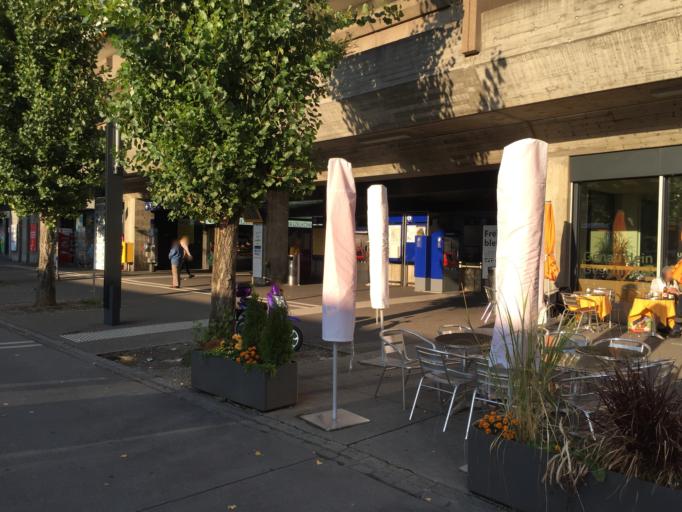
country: CH
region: Zurich
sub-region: Bezirk Dietikon
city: Dietikon
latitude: 47.4059
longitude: 8.4044
